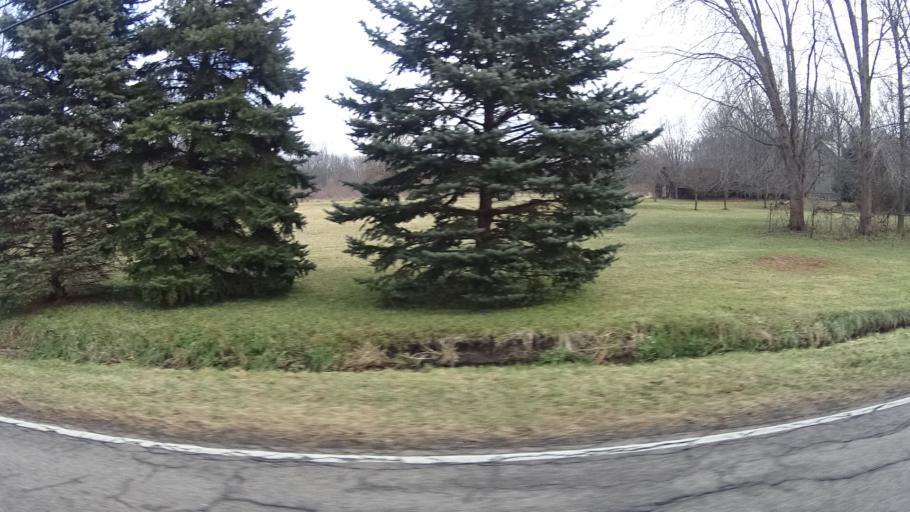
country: US
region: Ohio
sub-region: Lorain County
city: Amherst
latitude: 41.4039
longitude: -82.2015
